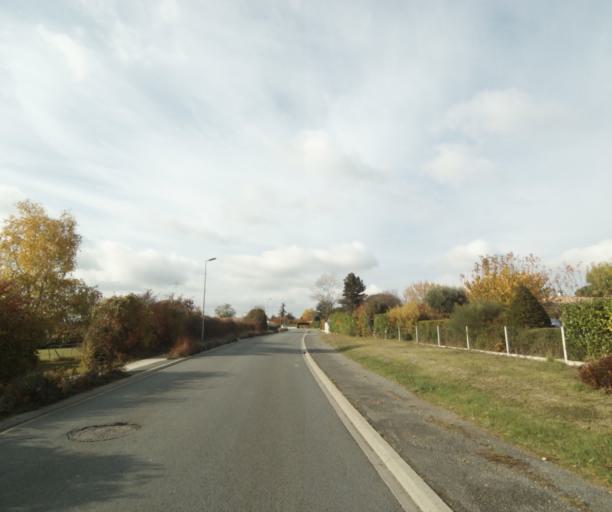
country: FR
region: Poitou-Charentes
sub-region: Departement de la Charente-Maritime
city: Saint-Georges-des-Coteaux
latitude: 45.7661
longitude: -0.7057
